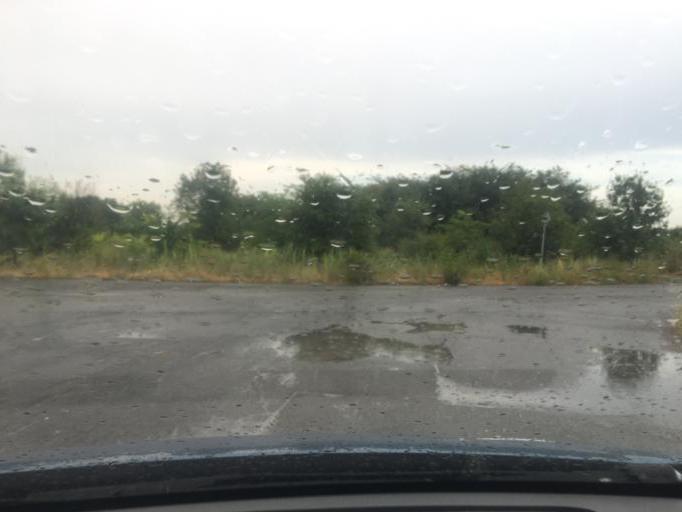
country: BG
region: Burgas
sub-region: Obshtina Burgas
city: Burgas
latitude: 42.5537
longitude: 27.4880
